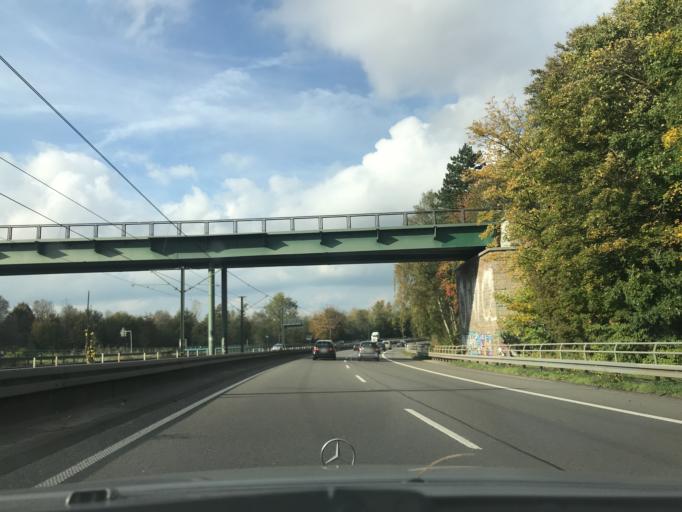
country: DE
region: North Rhine-Westphalia
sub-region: Regierungsbezirk Arnsberg
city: Dortmund
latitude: 51.4858
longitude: 7.4684
